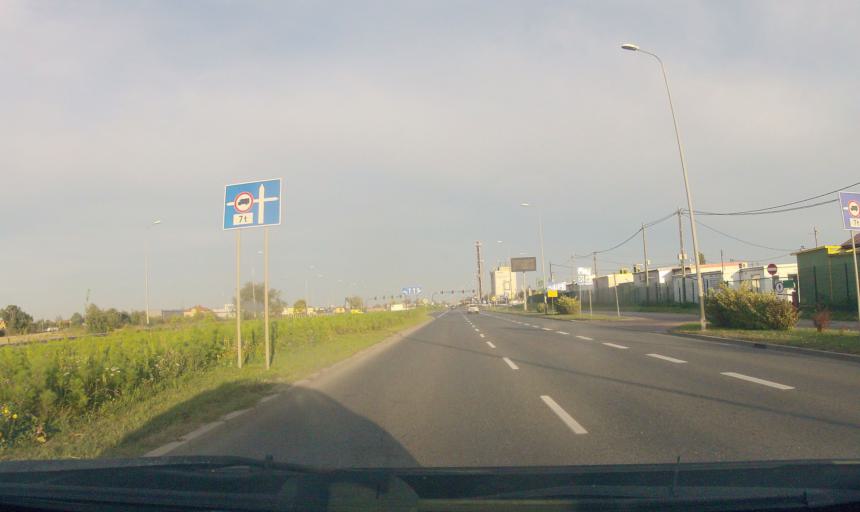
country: PL
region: Lesser Poland Voivodeship
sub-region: Powiat wielicki
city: Czarnochowice
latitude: 50.0381
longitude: 20.0405
